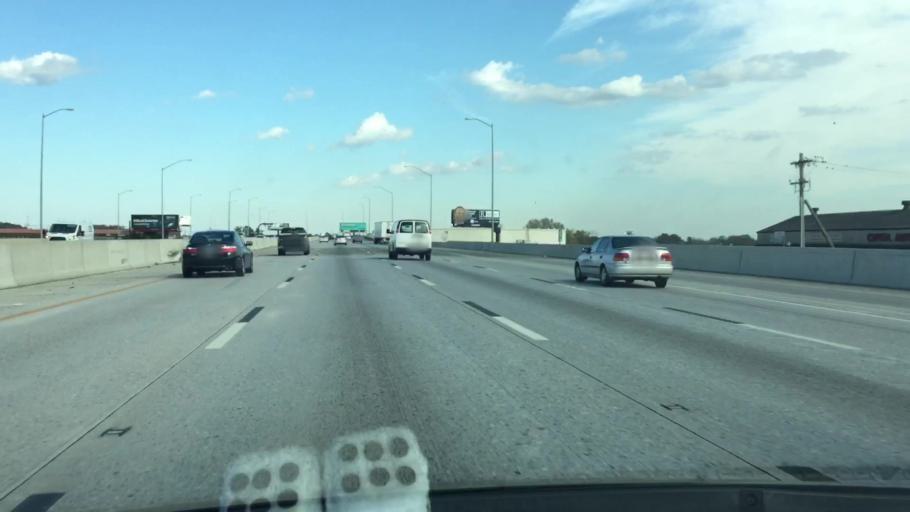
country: US
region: New Jersey
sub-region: Burlington County
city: Palmyra
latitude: 40.0253
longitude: -75.0278
